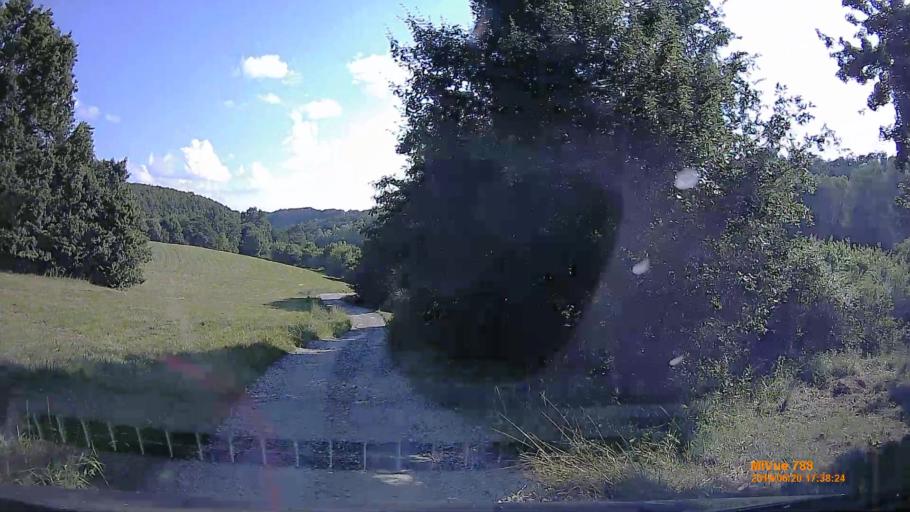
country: HU
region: Baranya
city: Buekkoesd
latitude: 46.1413
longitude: 18.0073
